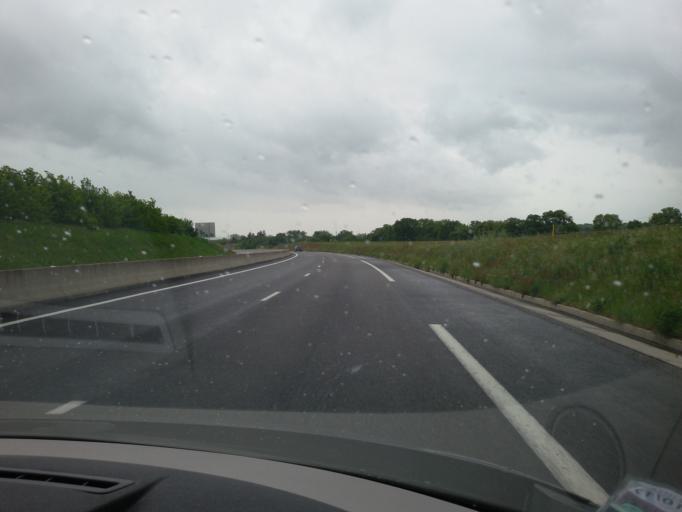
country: FR
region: Rhone-Alpes
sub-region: Departement de la Drome
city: Bourg-les-Valence
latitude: 44.9559
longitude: 4.9310
